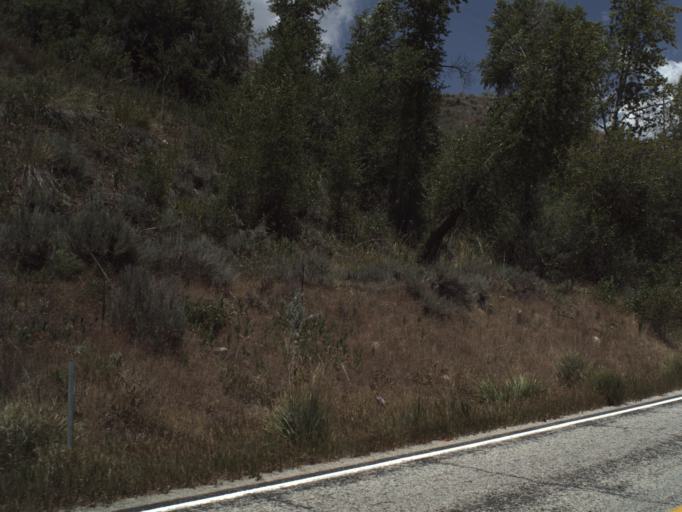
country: US
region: Utah
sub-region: Weber County
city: Wolf Creek
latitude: 41.2912
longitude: -111.6372
